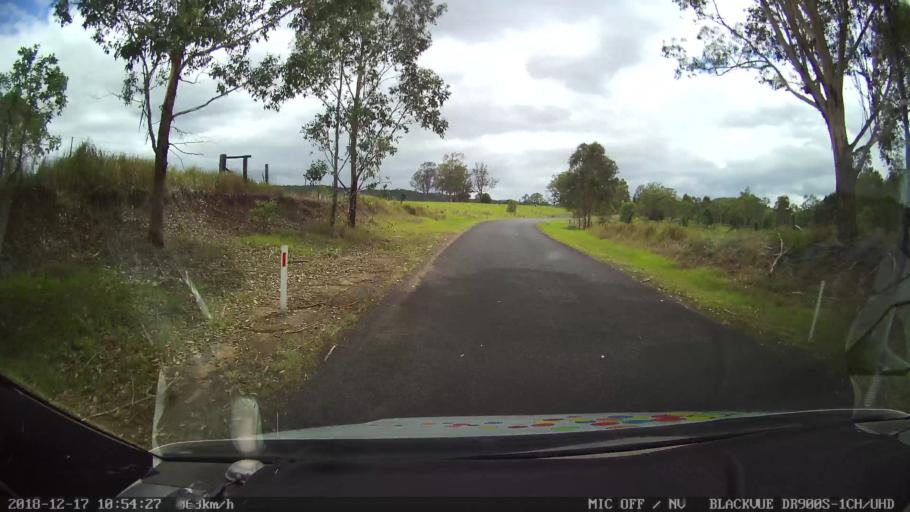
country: AU
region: New South Wales
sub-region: Tenterfield Municipality
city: Carrolls Creek
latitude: -28.8291
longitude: 152.5673
